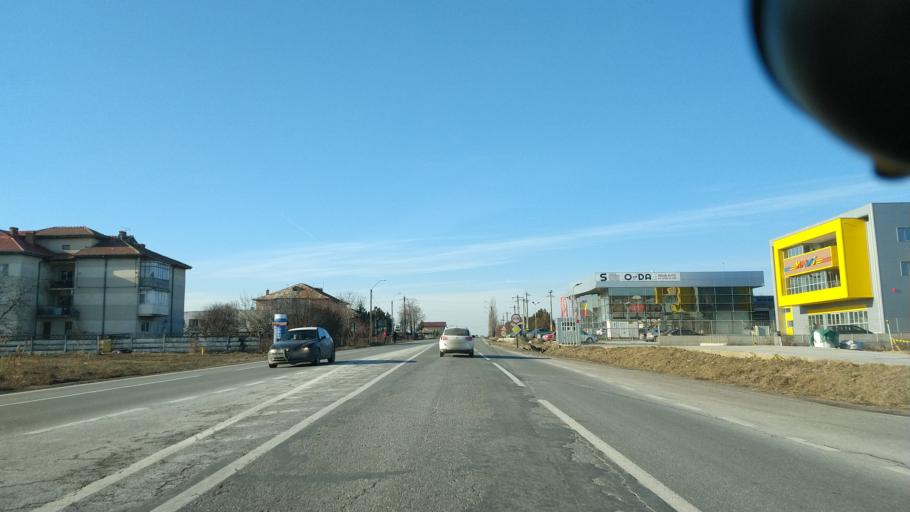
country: RO
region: Iasi
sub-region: Comuna Letcani
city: Letcani
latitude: 47.1850
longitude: 27.4539
